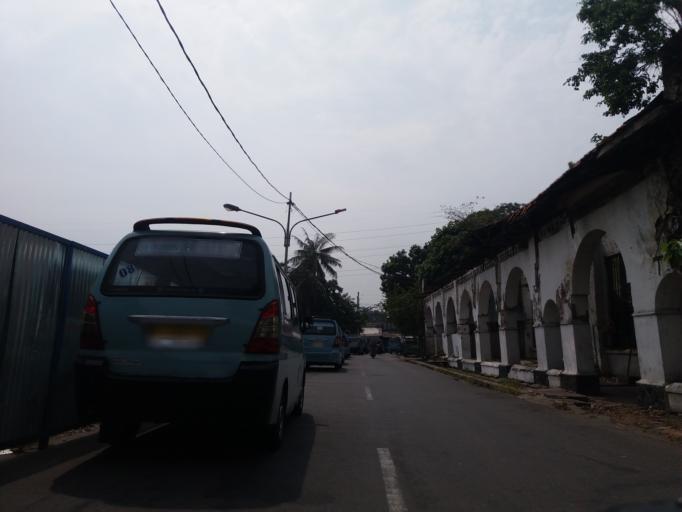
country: ID
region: Jakarta Raya
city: Jakarta
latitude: -6.1320
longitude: 106.8111
